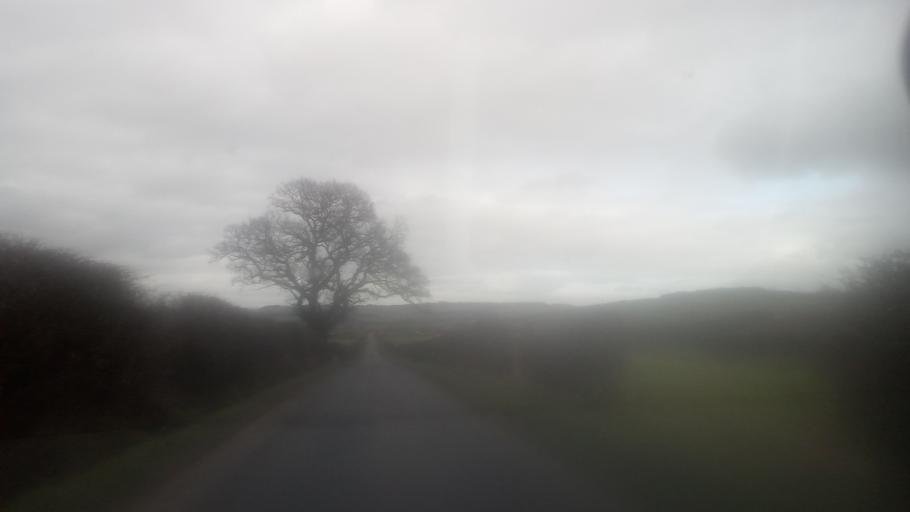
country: GB
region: Scotland
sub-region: The Scottish Borders
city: Jedburgh
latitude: 55.5056
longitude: -2.4779
